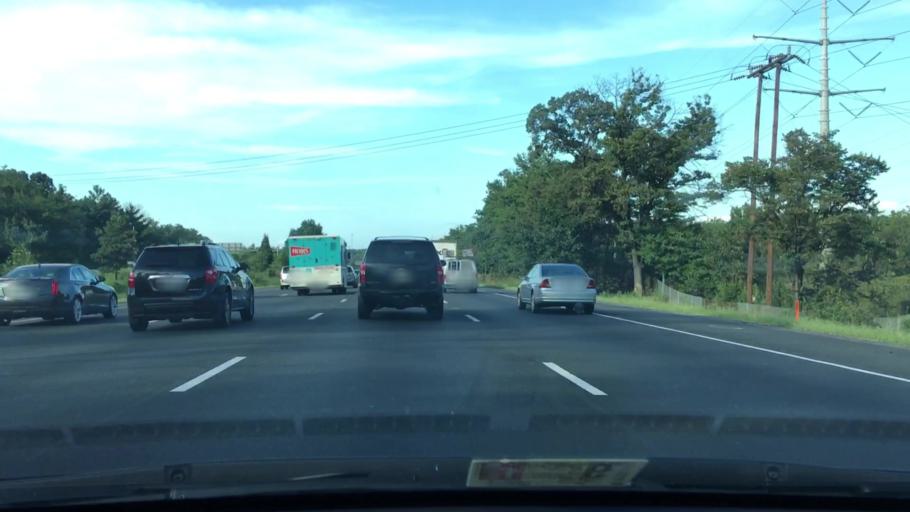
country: US
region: Maryland
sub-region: Prince George's County
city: Calverton
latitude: 39.0393
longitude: -76.9370
